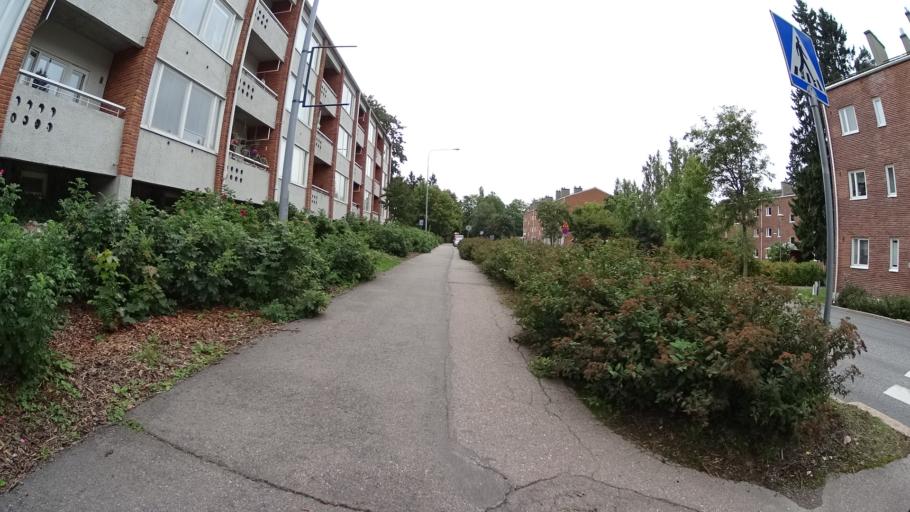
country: FI
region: Uusimaa
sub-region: Helsinki
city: Helsinki
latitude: 60.2296
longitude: 24.9228
